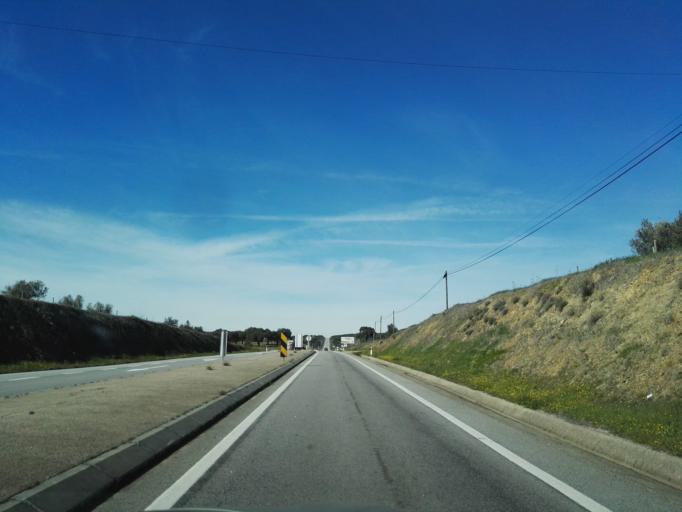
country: PT
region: Portalegre
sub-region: Arronches
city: Arronches
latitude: 39.1347
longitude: -7.2910
